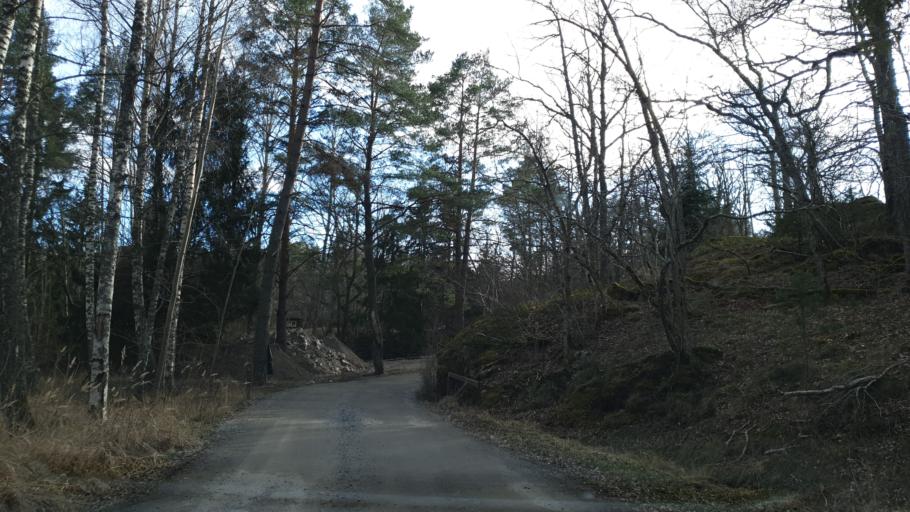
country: SE
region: Stockholm
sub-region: Varmdo Kommun
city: Holo
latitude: 59.3718
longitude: 18.6753
